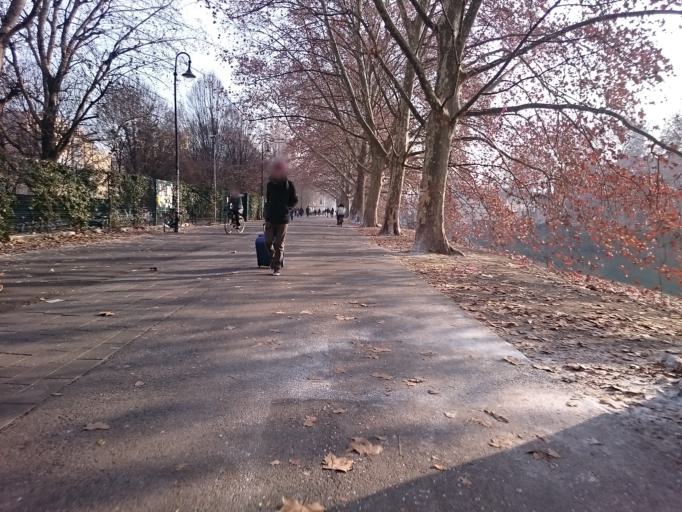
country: IT
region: Veneto
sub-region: Provincia di Padova
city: Padova
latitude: 45.4105
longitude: 11.8904
